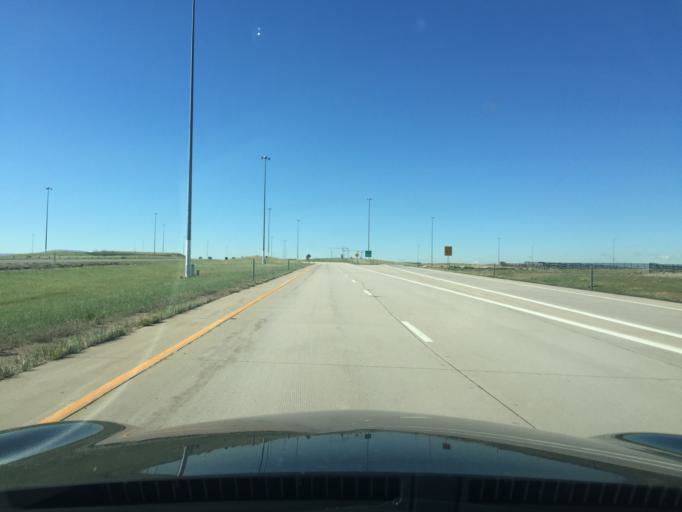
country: US
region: Colorado
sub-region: Adams County
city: Aurora
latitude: 39.8409
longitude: -104.7475
